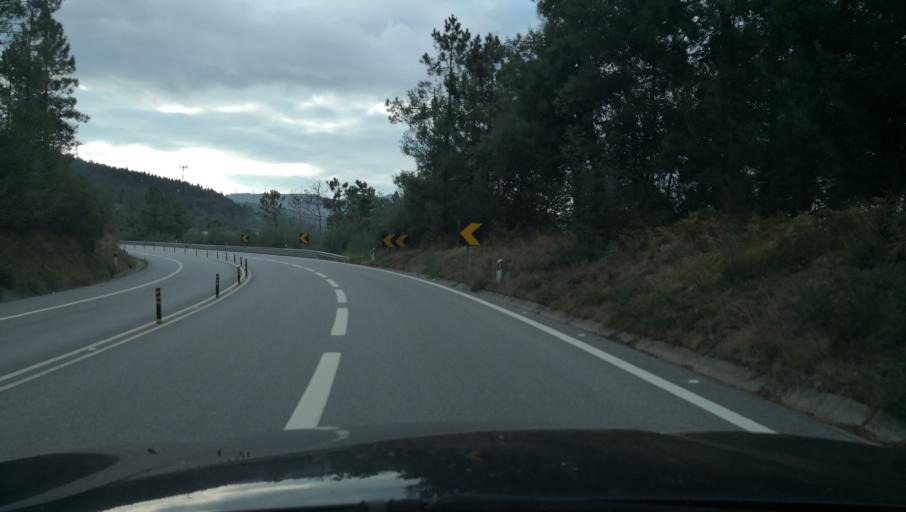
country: PT
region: Vila Real
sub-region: Santa Marta de Penaguiao
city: Santa Marta de Penaguiao
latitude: 41.2811
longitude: -7.8674
